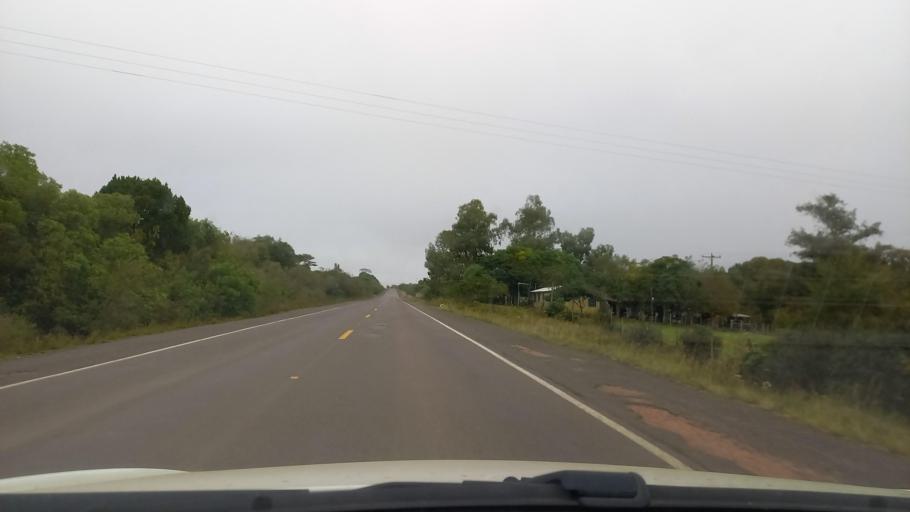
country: BR
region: Rio Grande do Sul
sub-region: Cacequi
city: Cacequi
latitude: -30.1227
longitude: -54.6433
